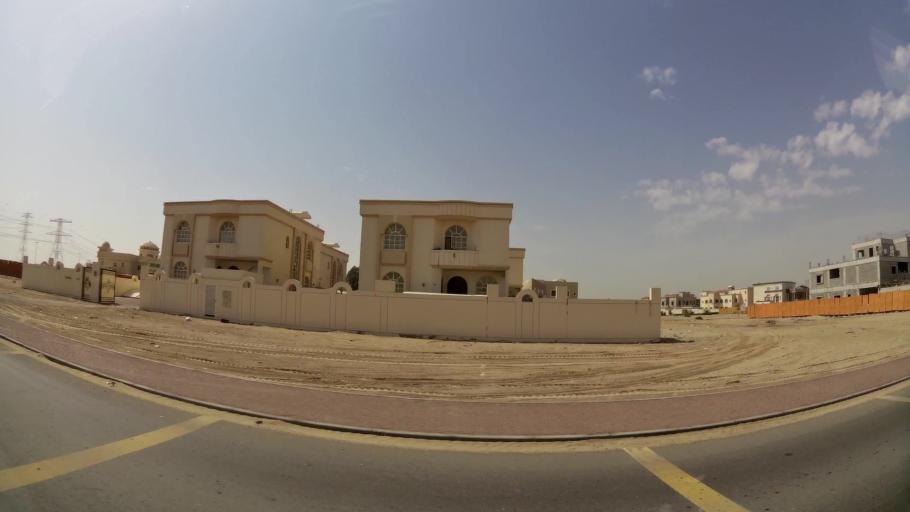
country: AE
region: Abu Dhabi
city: Abu Dhabi
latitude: 24.3098
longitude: 54.5748
